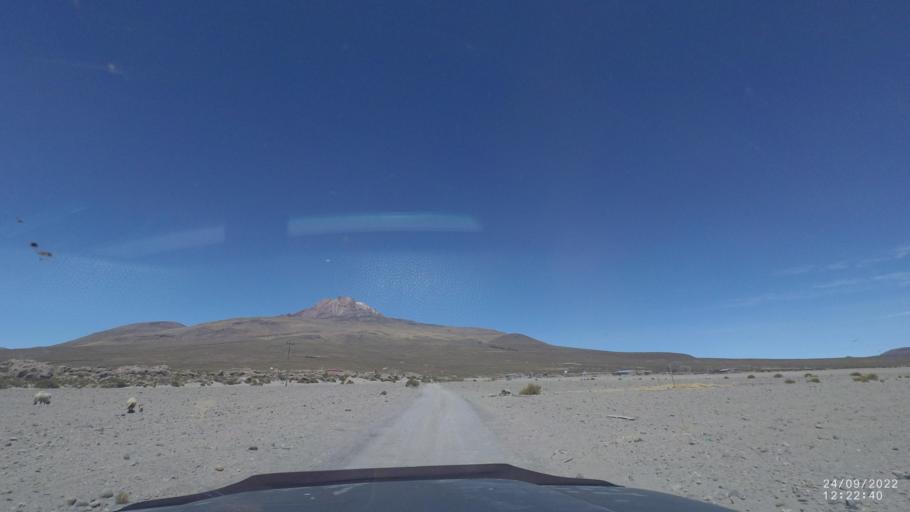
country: BO
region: Potosi
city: Colchani
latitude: -19.7581
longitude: -67.6645
